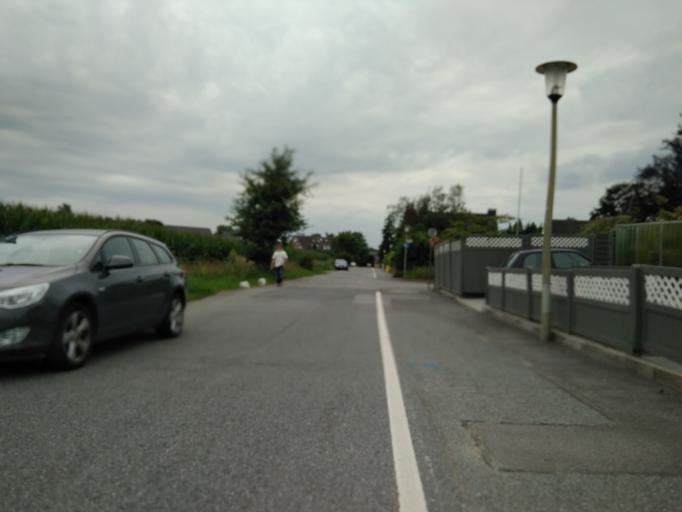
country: DE
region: North Rhine-Westphalia
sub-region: Regierungsbezirk Munster
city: Bottrop
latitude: 51.5912
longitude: 6.9173
